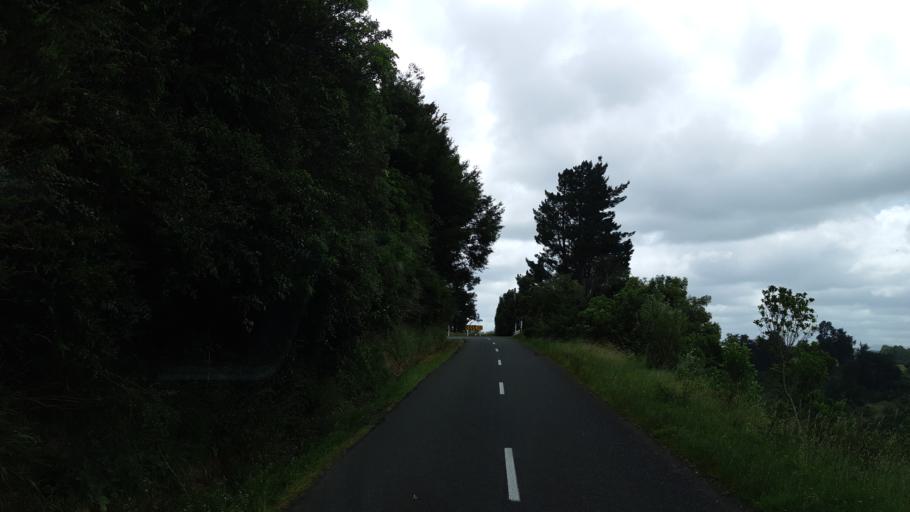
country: NZ
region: Manawatu-Wanganui
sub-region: Palmerston North City
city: Palmerston North
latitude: -39.9380
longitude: 175.9156
